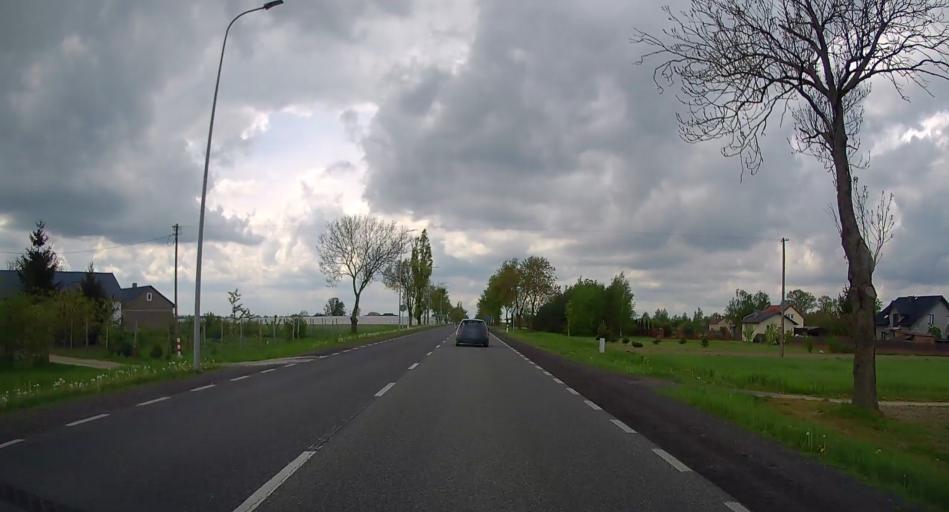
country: PL
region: Masovian Voivodeship
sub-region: Powiat plonski
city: Zaluski
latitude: 52.4422
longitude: 20.4890
